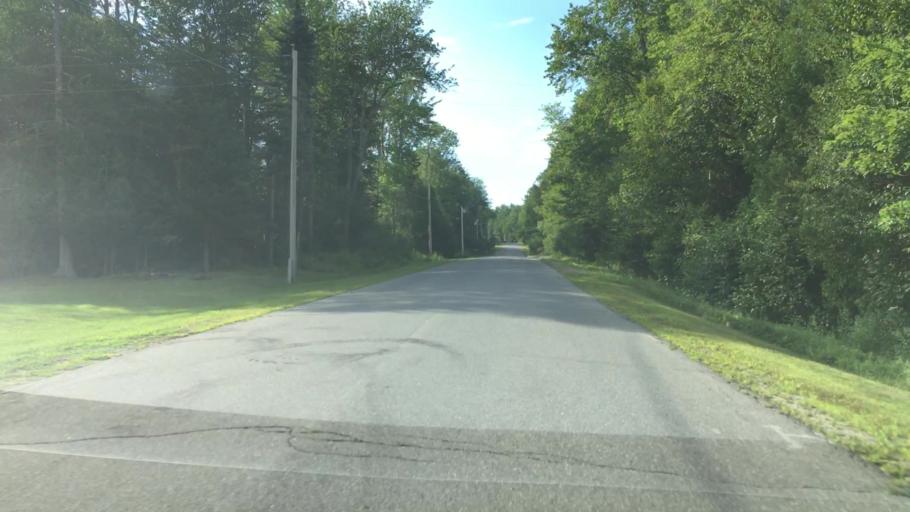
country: US
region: Maine
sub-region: Waldo County
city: Stockton Springs
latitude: 44.4895
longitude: -68.8657
